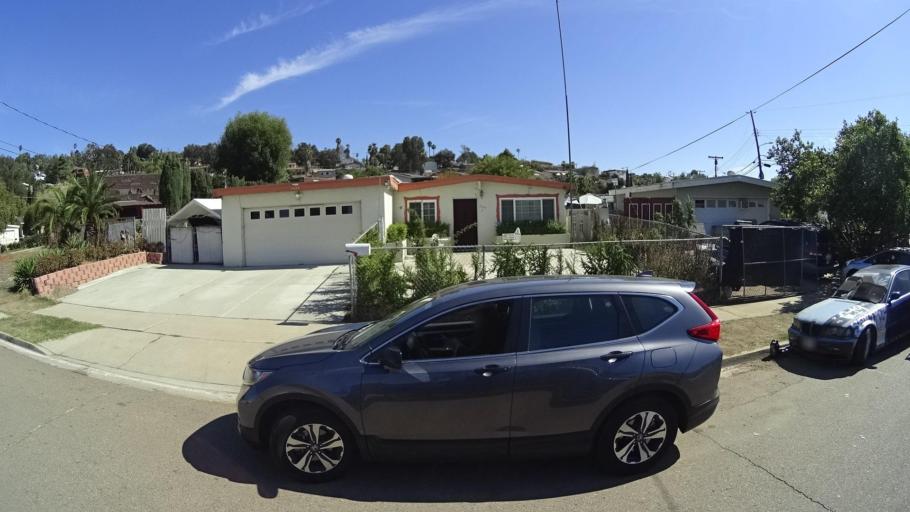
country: US
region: California
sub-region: San Diego County
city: La Presa
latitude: 32.7213
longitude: -117.0130
